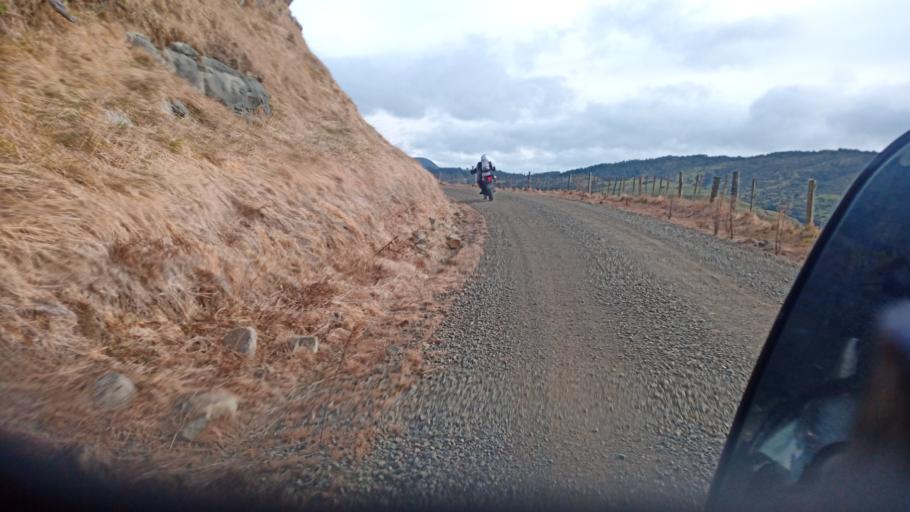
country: NZ
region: Gisborne
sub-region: Gisborne District
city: Gisborne
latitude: -38.4676
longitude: 177.5302
